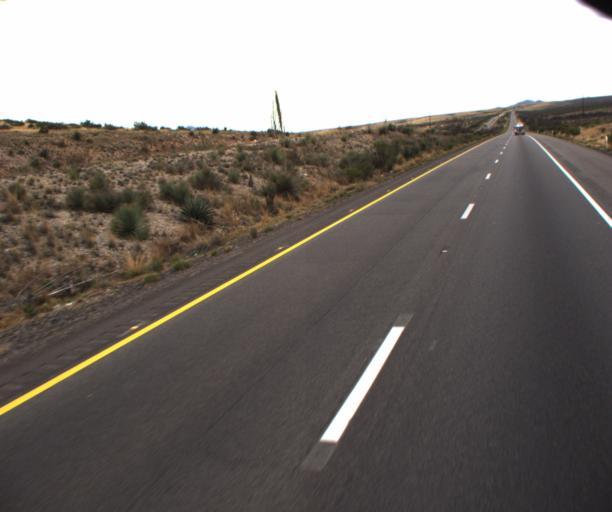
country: US
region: Arizona
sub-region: Cochise County
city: Willcox
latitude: 32.1135
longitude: -110.0222
